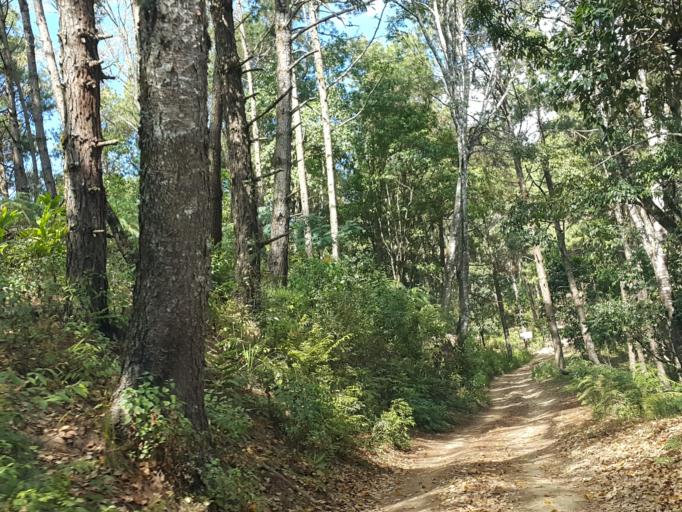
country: TH
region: Chiang Mai
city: Wiang Haeng
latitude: 19.5478
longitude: 98.8145
